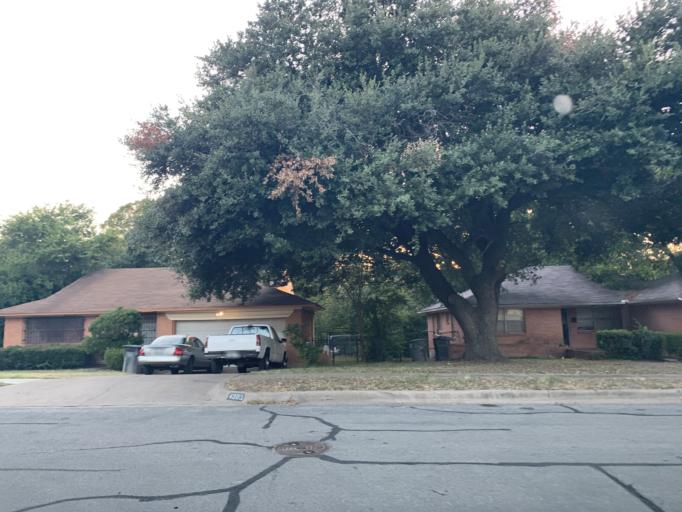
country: US
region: Texas
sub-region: Dallas County
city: Dallas
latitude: 32.6950
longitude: -96.8091
